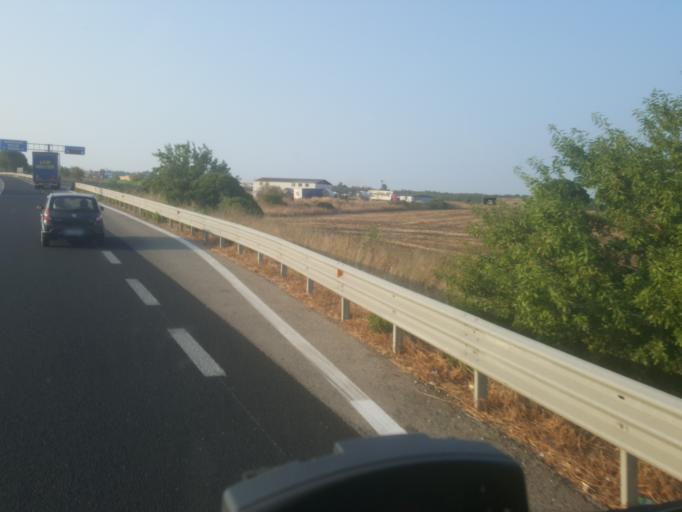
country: IT
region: Latium
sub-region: Citta metropolitana di Roma Capitale
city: Aurelia
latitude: 42.1585
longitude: 11.7890
